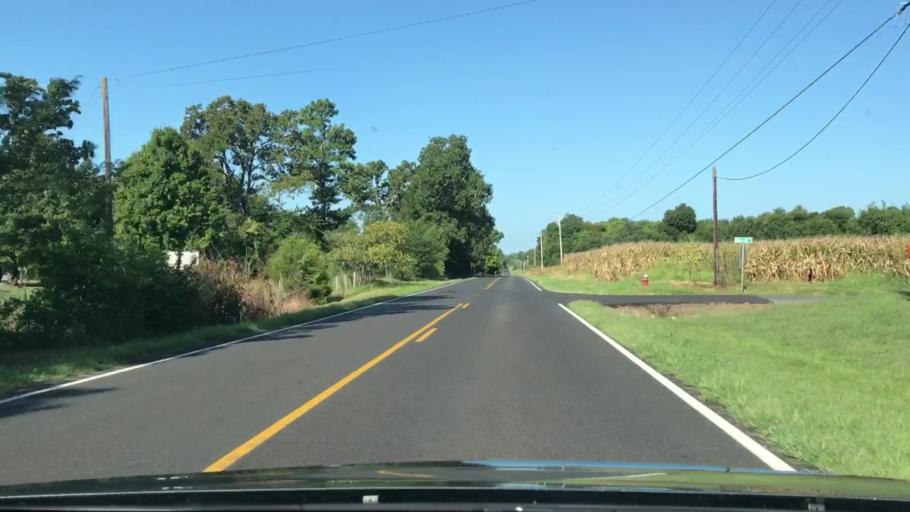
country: US
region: Kentucky
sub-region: Marshall County
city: Benton
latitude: 36.7647
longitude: -88.3197
